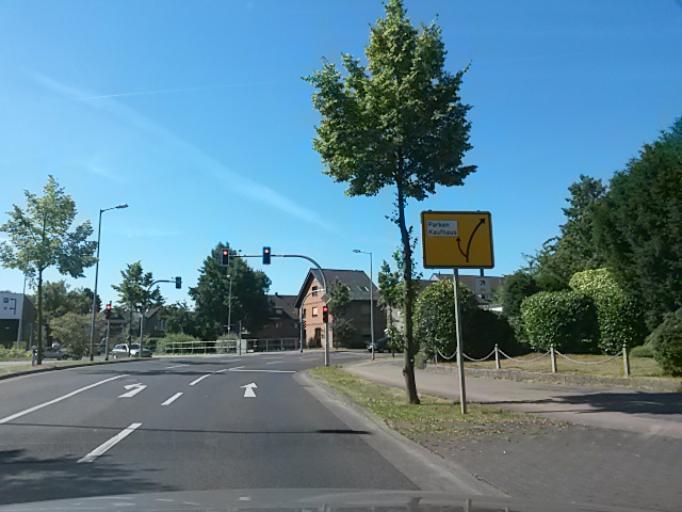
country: DE
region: North Rhine-Westphalia
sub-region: Regierungsbezirk Dusseldorf
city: Nettetal
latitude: 51.3061
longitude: 6.2719
